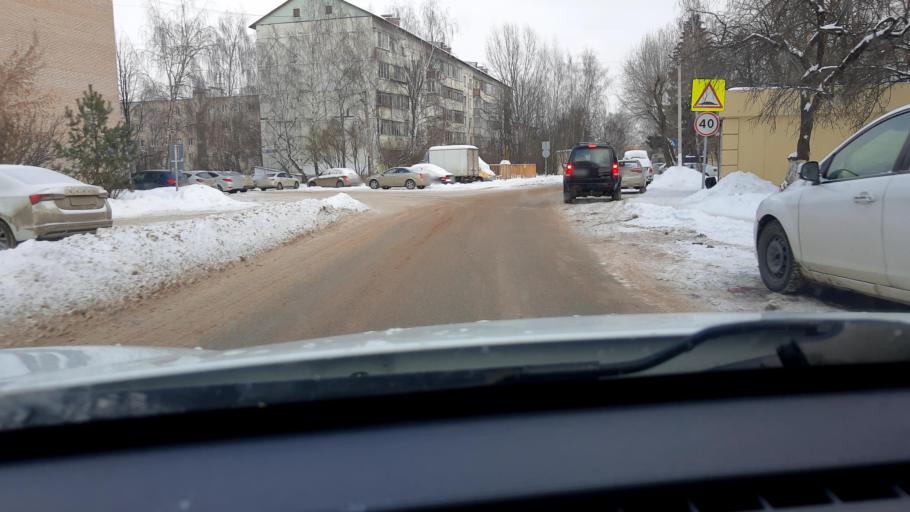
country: RU
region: Moskovskaya
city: Pavlovskaya Sloboda
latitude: 55.8177
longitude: 37.0871
